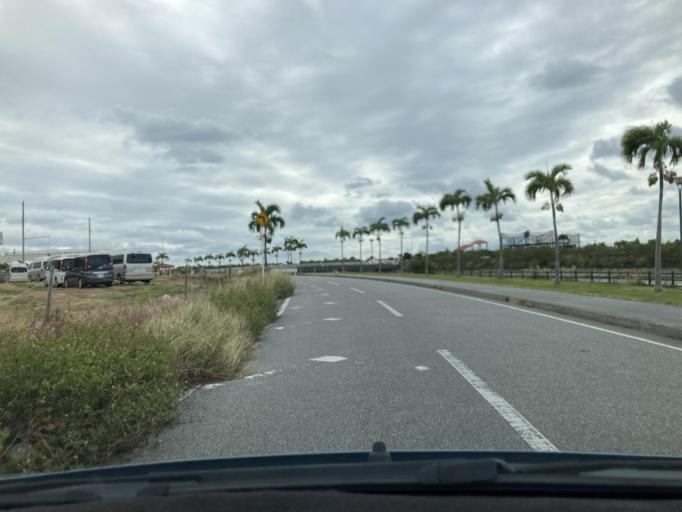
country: JP
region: Okinawa
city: Itoman
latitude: 26.1587
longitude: 127.6496
